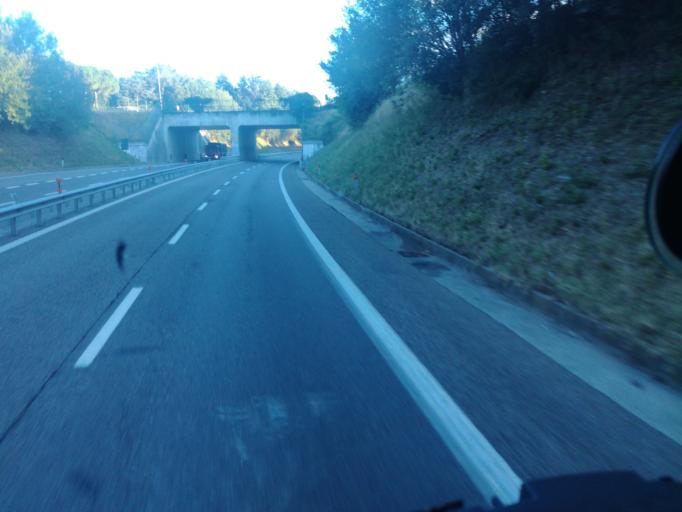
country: IT
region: Lombardy
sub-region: Provincia di Monza e Brianza
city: Lentate sul Seveso
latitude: 45.6746
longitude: 9.1110
